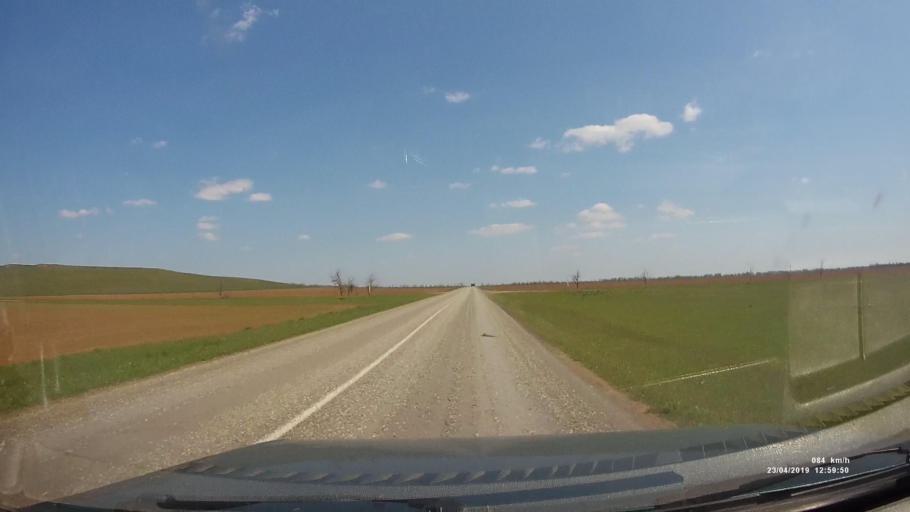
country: RU
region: Kalmykiya
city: Yashalta
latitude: 46.6041
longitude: 42.6227
